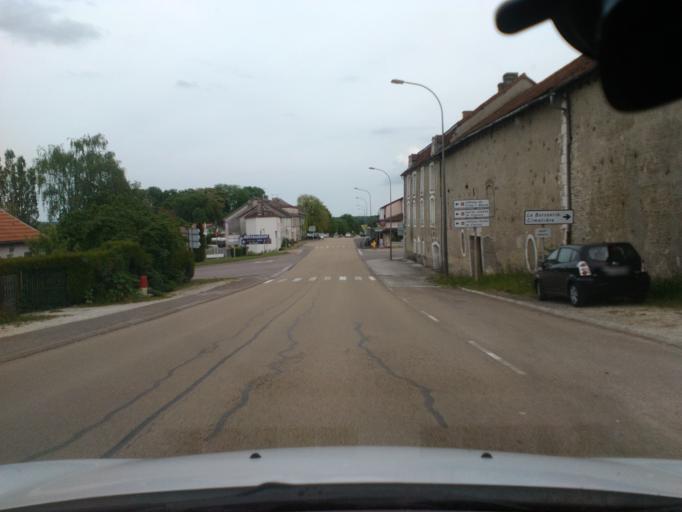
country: FR
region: Champagne-Ardenne
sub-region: Departement de la Haute-Marne
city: Lavilleneuve-au-Roi
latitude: 48.2258
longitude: 4.8870
